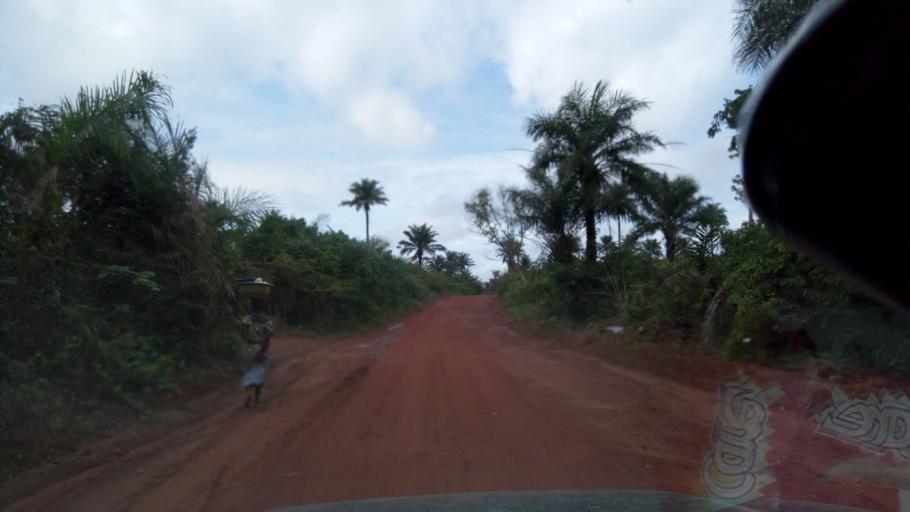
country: SL
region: Northern Province
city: Pepel
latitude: 8.6746
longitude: -13.0006
